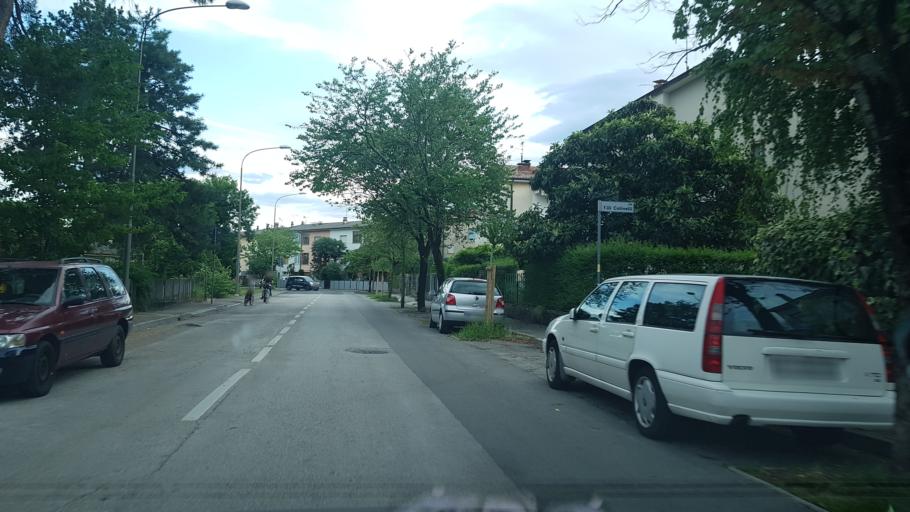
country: IT
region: Friuli Venezia Giulia
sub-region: Provincia di Gorizia
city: Gorizia
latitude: 45.9282
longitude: 13.6168
